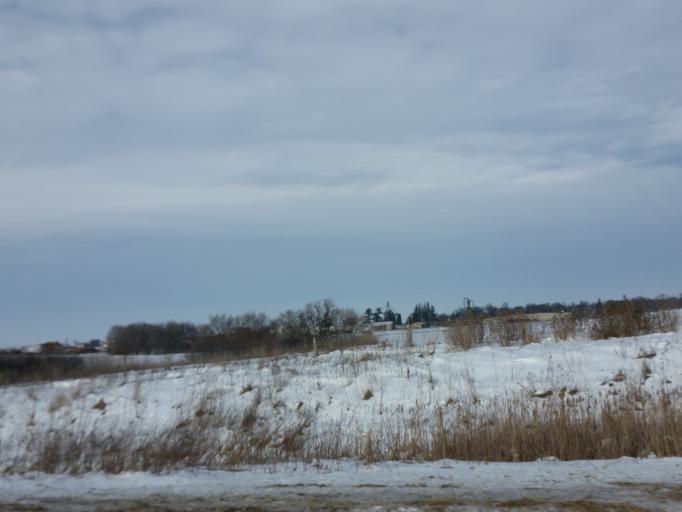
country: US
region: Iowa
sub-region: Buchanan County
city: Independence
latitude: 42.4617
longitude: -91.7390
